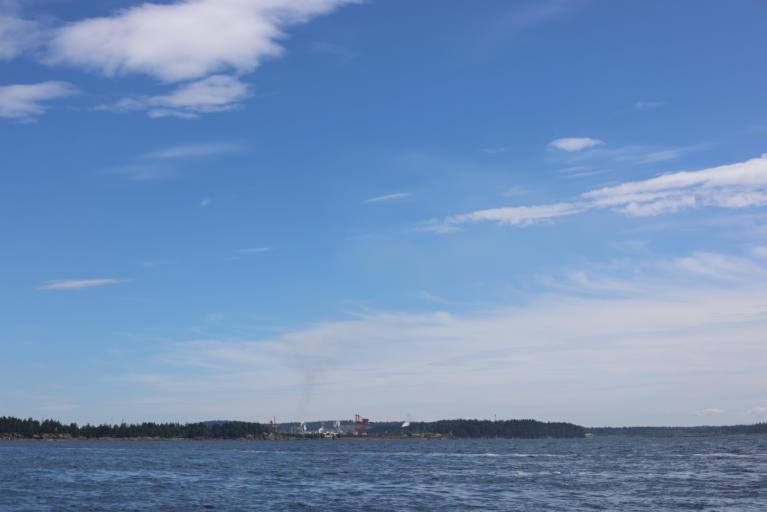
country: CA
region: British Columbia
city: Nanaimo
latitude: 49.1649
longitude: -123.9194
